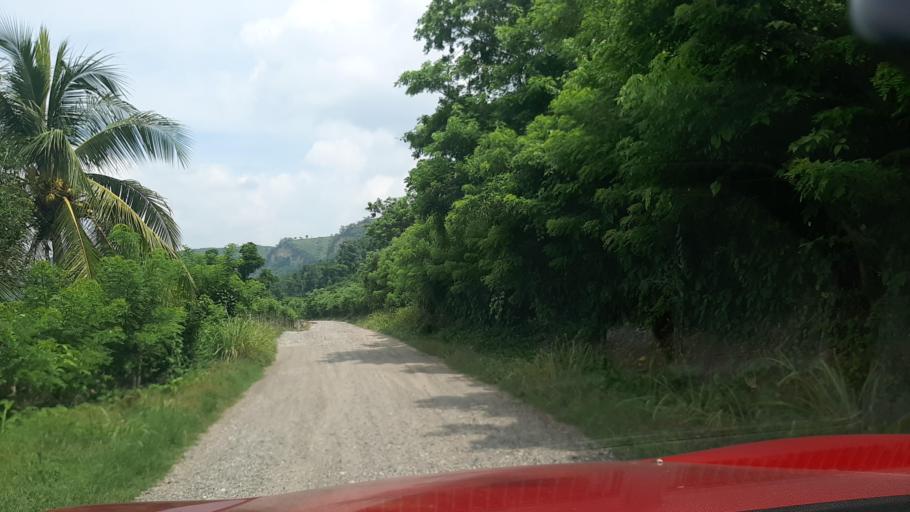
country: MX
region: Veracruz
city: Gutierrez Zamora
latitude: 20.4588
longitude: -97.1815
